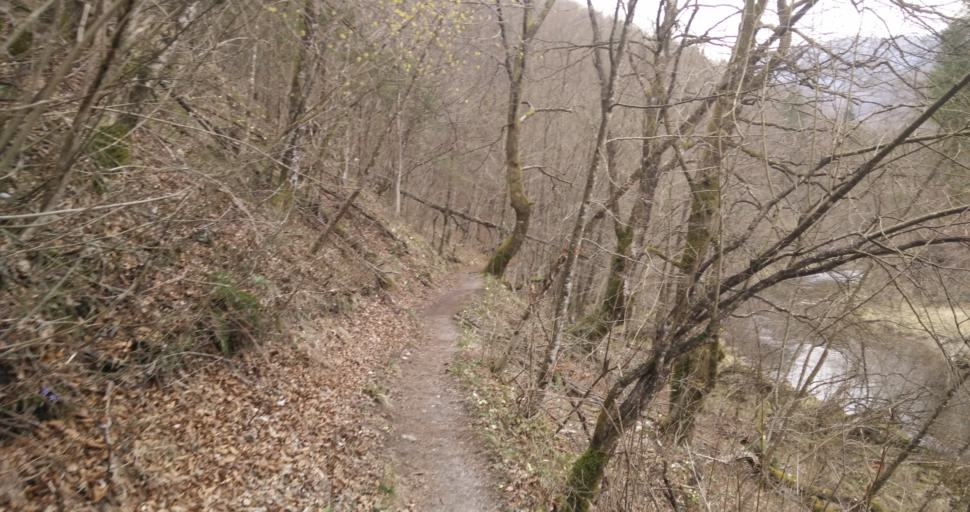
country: HR
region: Primorsko-Goranska
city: Vrbovsko
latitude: 45.3561
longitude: 15.0635
